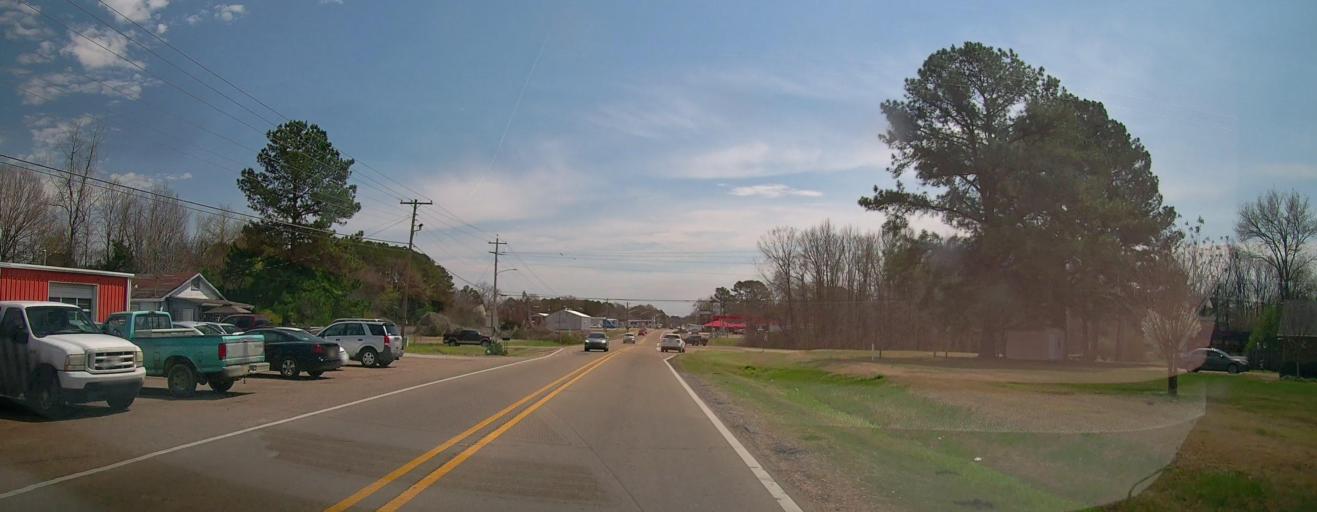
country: US
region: Mississippi
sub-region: Union County
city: New Albany
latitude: 34.5120
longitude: -89.0383
